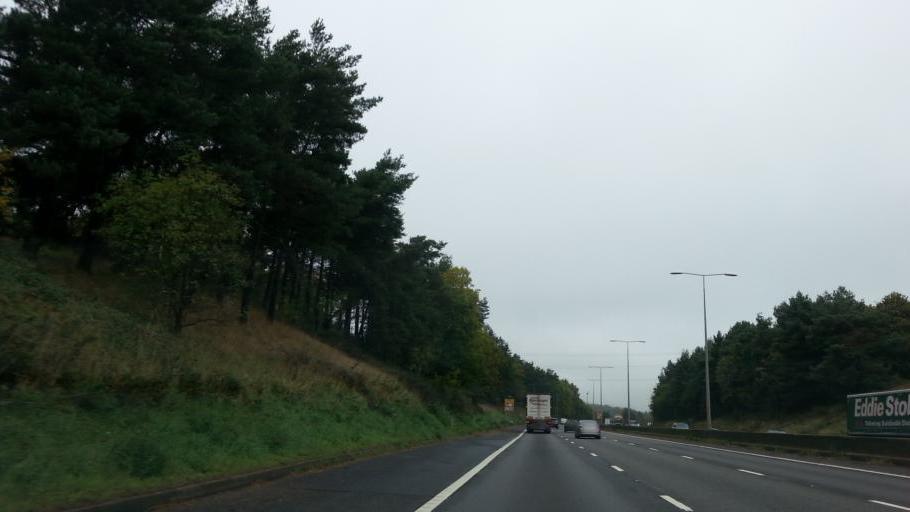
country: GB
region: England
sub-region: Worcestershire
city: Barnt Green
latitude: 52.3916
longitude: -2.0522
